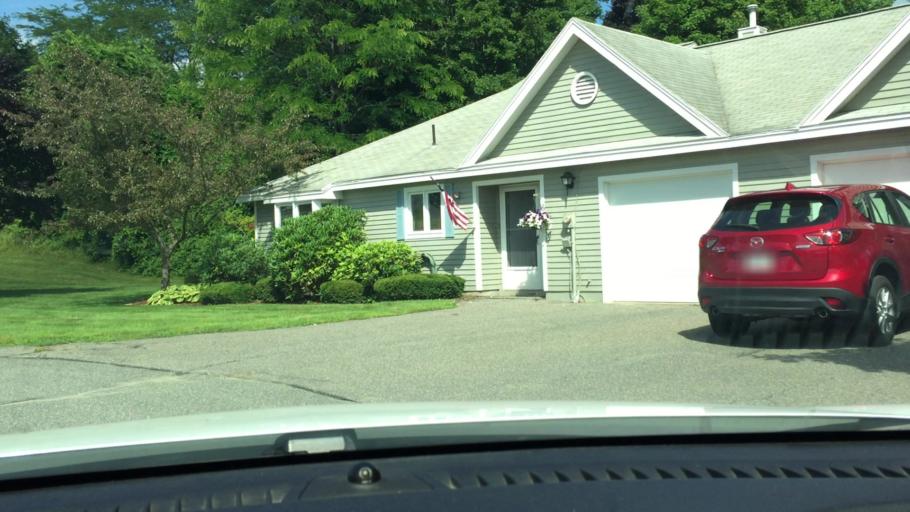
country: US
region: Massachusetts
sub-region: Berkshire County
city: Pittsfield
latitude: 42.4544
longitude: -73.2807
